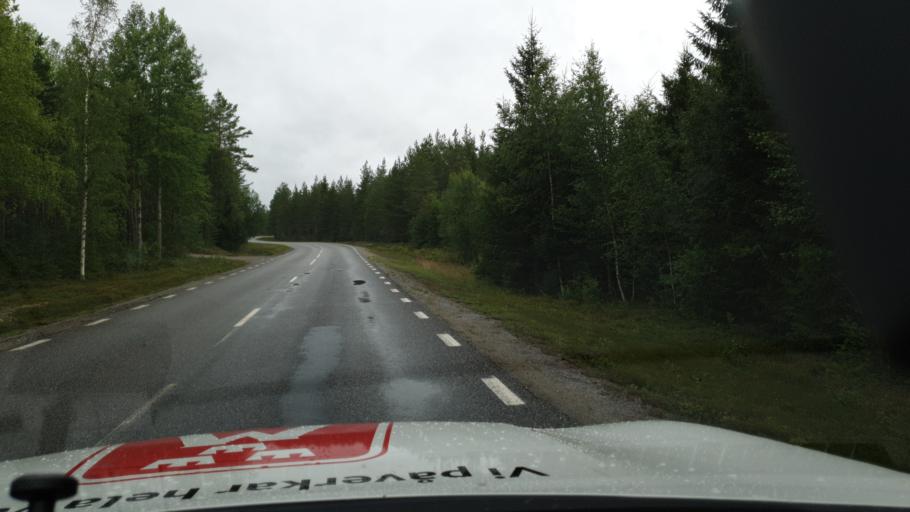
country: SE
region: Vaesterbotten
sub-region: Umea Kommun
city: Saevar
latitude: 63.9211
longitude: 20.5399
